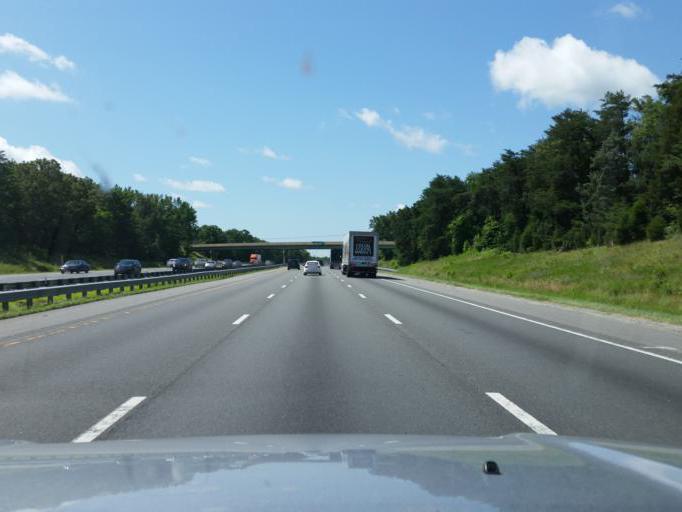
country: US
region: Virginia
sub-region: Spotsylvania County
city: Spotsylvania Courthouse
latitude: 38.1814
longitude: -77.5018
